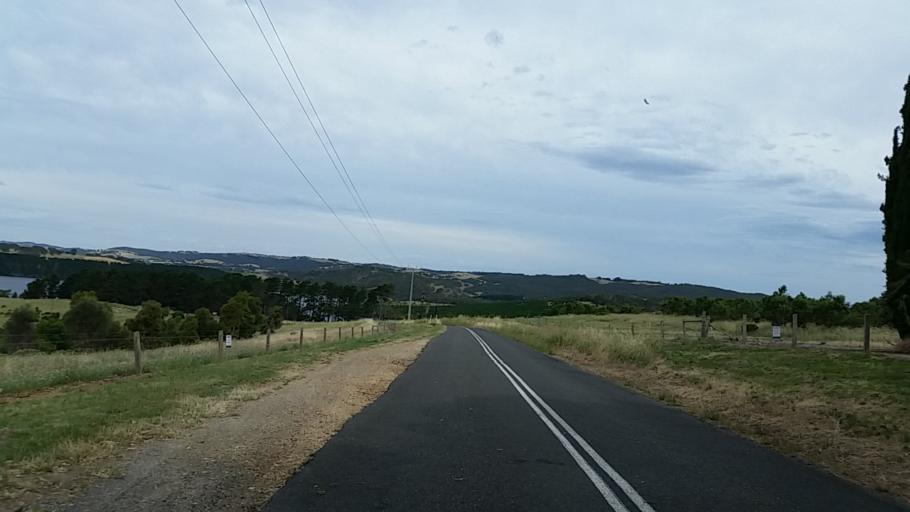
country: AU
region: South Australia
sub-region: Yankalilla
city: Normanville
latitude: -35.4030
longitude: 138.4131
